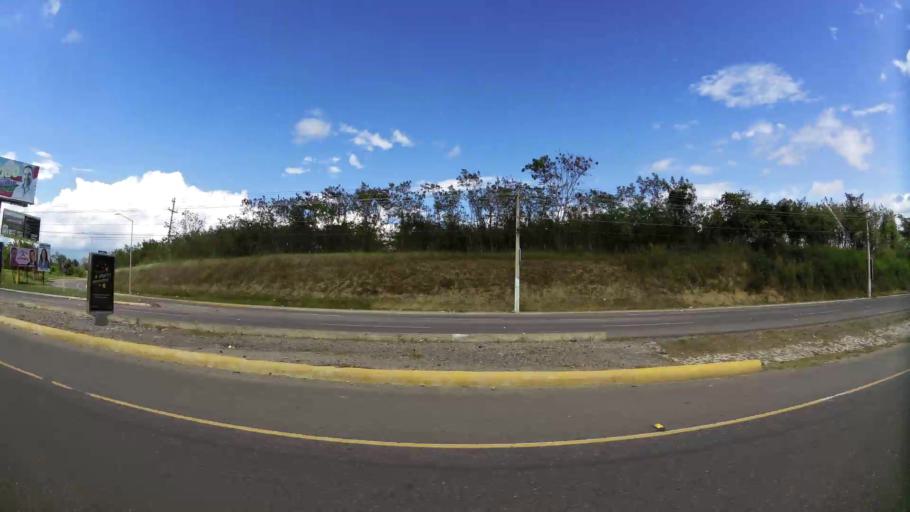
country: DO
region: Santiago
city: Licey al Medio
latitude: 19.3804
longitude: -70.6109
